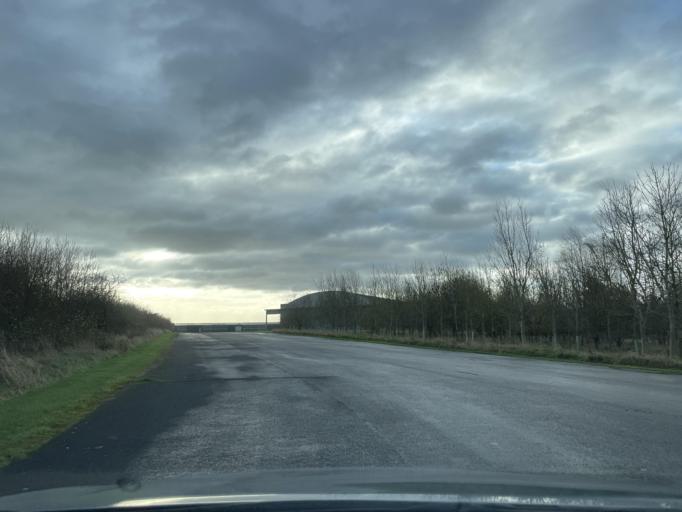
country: GB
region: England
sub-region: Borough of Swindon
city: Wroughton
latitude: 51.5148
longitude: -1.7970
